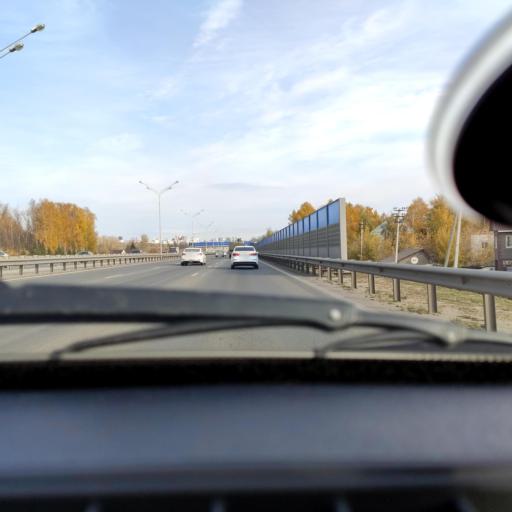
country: RU
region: Bashkortostan
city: Ufa
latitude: 54.6921
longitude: 55.9411
